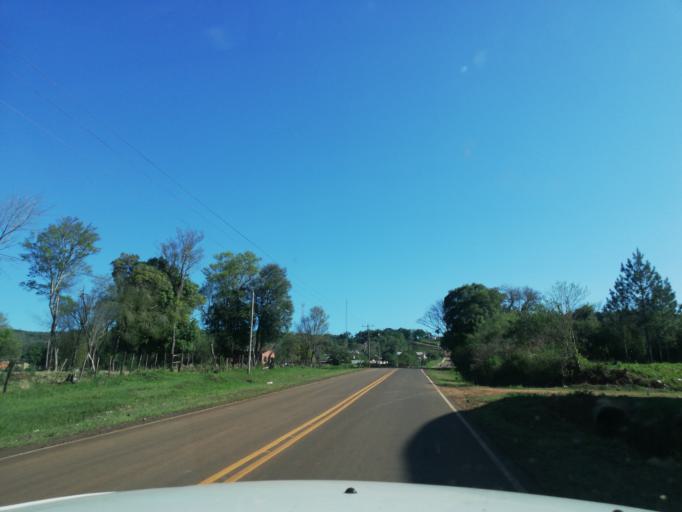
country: AR
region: Misiones
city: Arroyo del Medio
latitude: -27.6937
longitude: -55.4020
